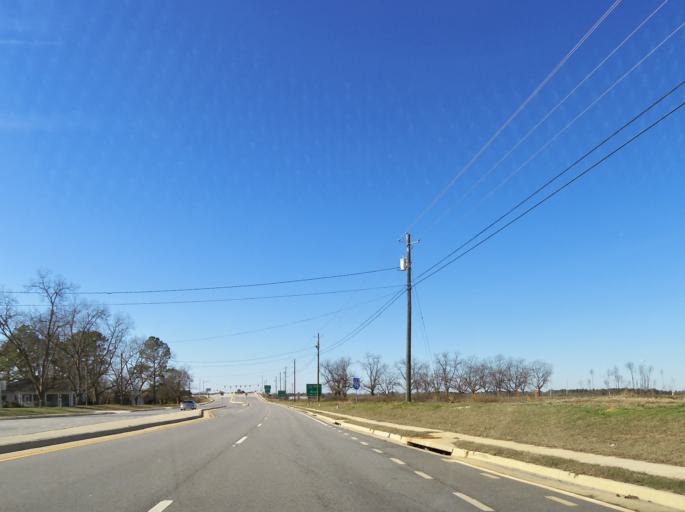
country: US
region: Georgia
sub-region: Peach County
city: Byron
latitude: 32.7169
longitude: -83.7236
